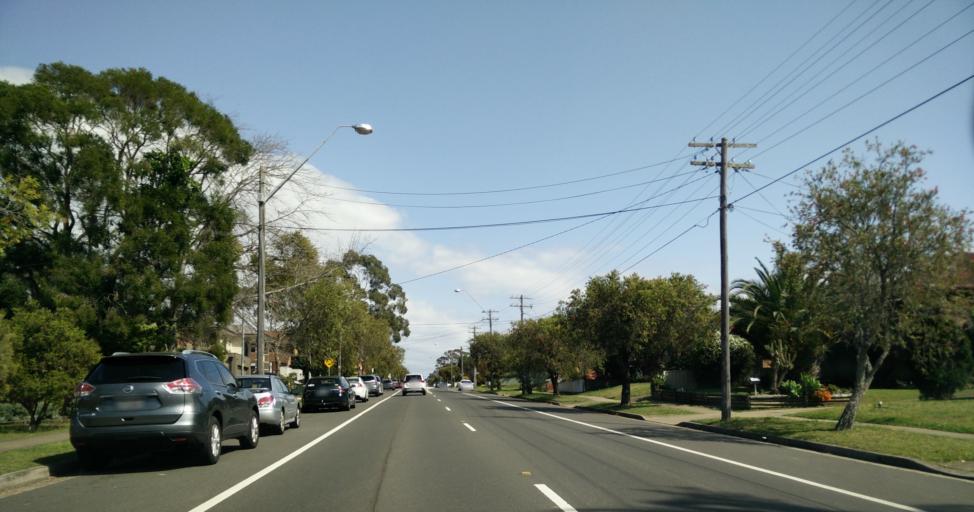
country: AU
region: New South Wales
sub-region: Bankstown
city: Revesby
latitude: -33.9581
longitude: 151.0131
